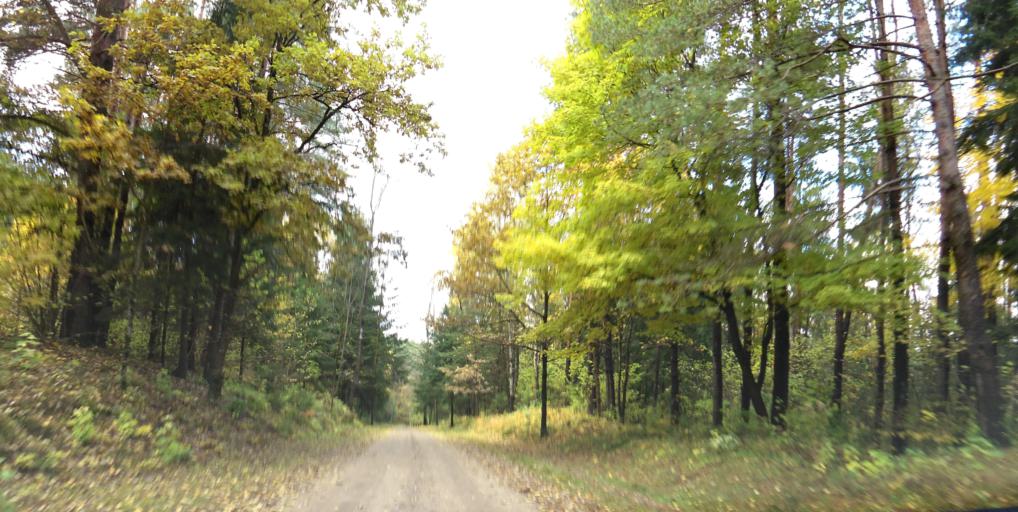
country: LT
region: Vilnius County
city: Vilkpede
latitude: 54.6493
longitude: 25.2541
